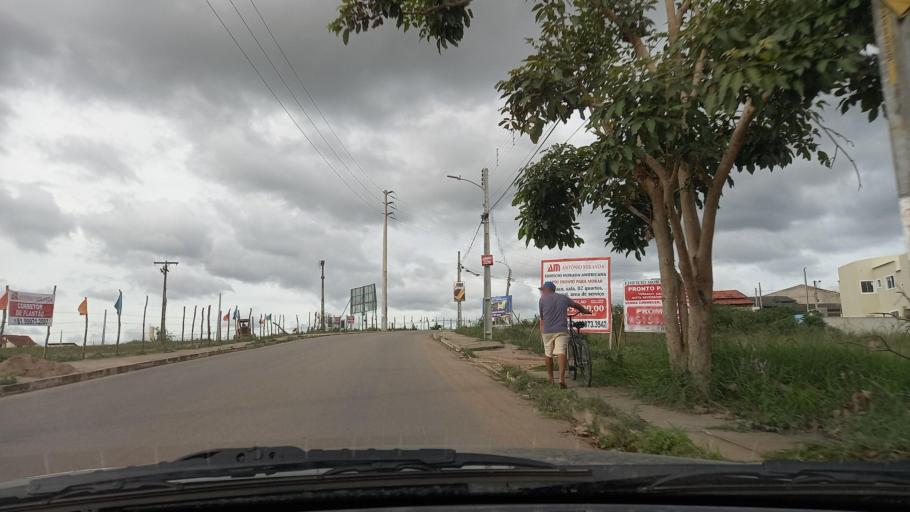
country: BR
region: Pernambuco
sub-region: Gravata
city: Gravata
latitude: -8.2027
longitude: -35.5508
